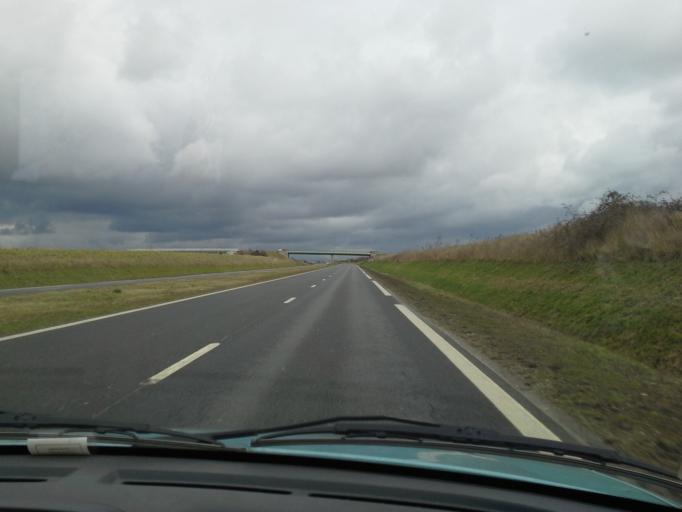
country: FR
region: Centre
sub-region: Departement du Loir-et-Cher
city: Villebarou
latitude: 47.6158
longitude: 1.3134
